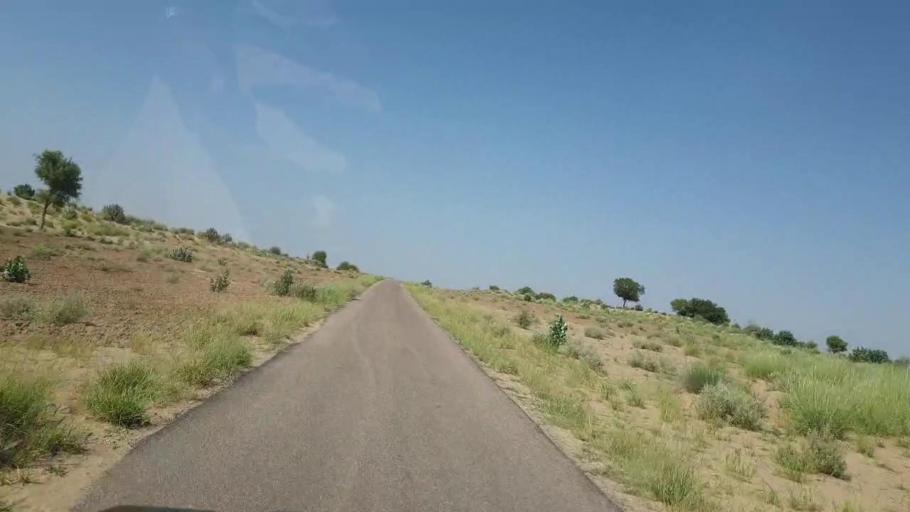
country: PK
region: Sindh
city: Chor
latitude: 25.6328
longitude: 70.3174
